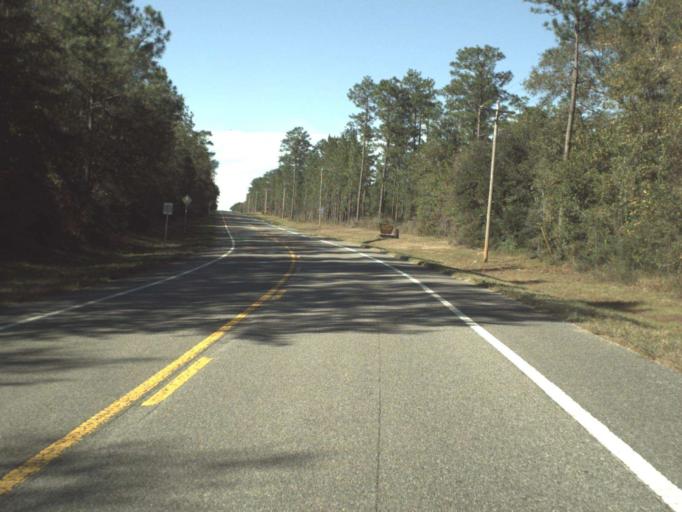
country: US
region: Florida
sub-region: Okaloosa County
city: Crestview
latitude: 30.8418
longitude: -86.7372
